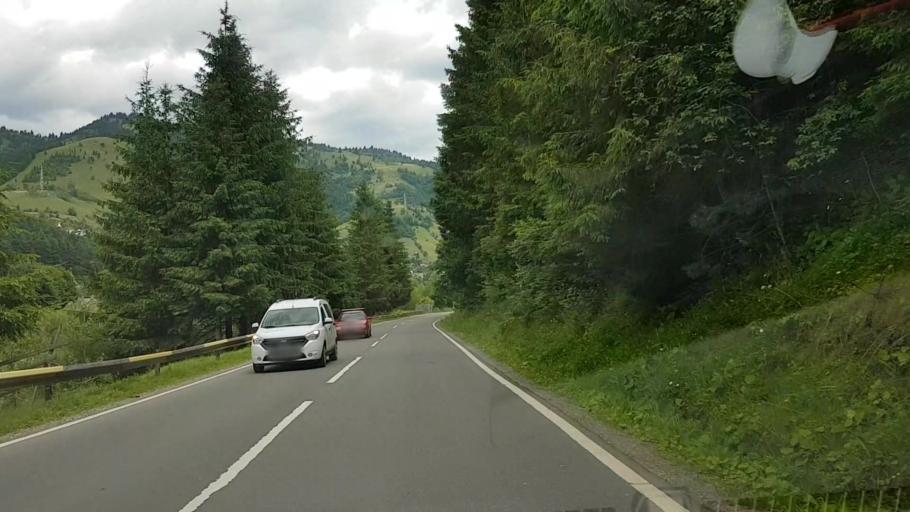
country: RO
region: Neamt
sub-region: Comuna Borca
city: Borca
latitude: 47.1973
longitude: 25.7564
